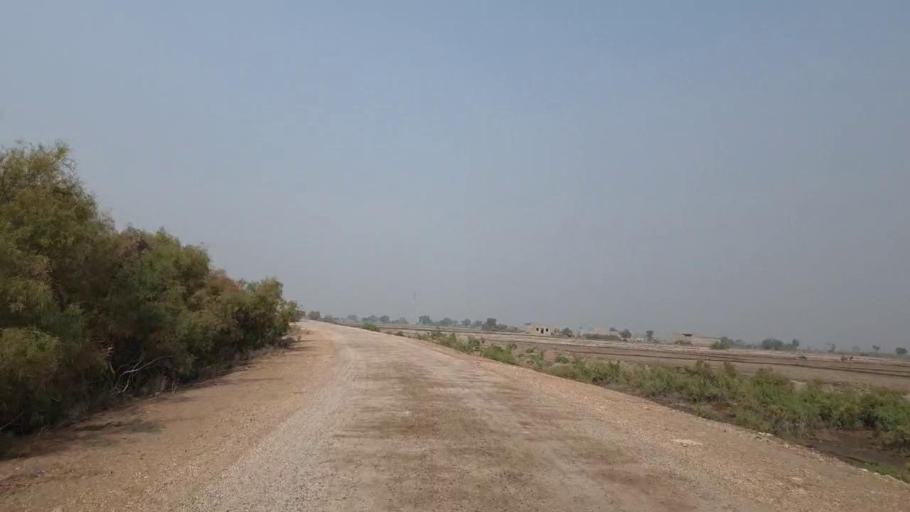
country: PK
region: Sindh
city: Bhan
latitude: 26.4907
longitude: 67.7006
